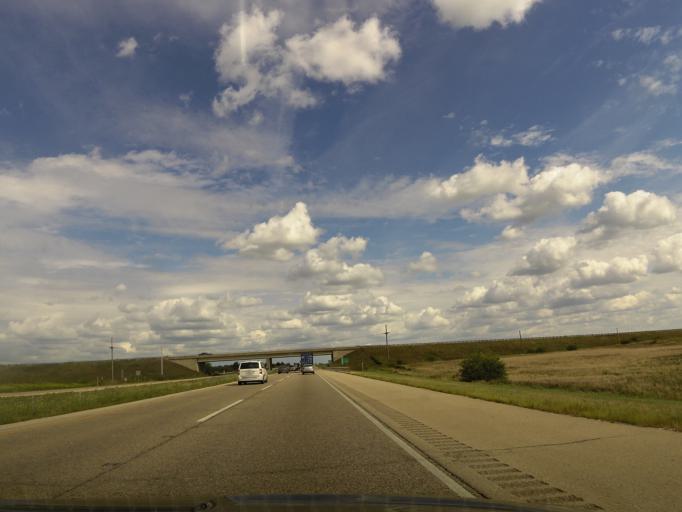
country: US
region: Illinois
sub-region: Kane County
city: Maple Park
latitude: 41.8735
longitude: -88.6040
